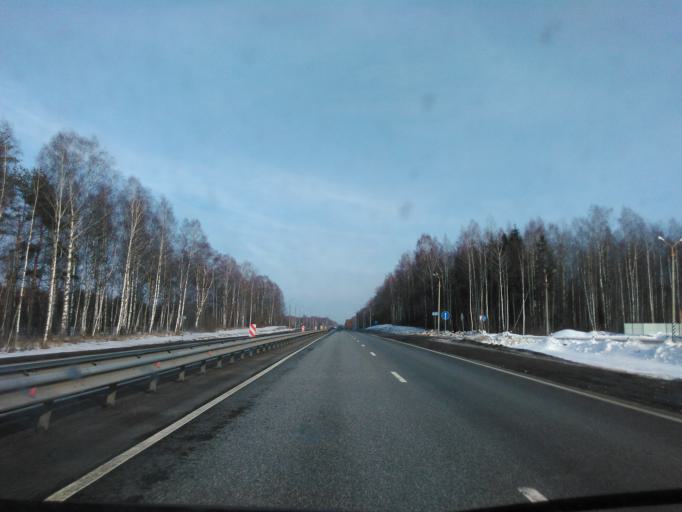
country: RU
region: Smolensk
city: Kholm-Zhirkovskiy
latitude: 55.1895
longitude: 33.7622
